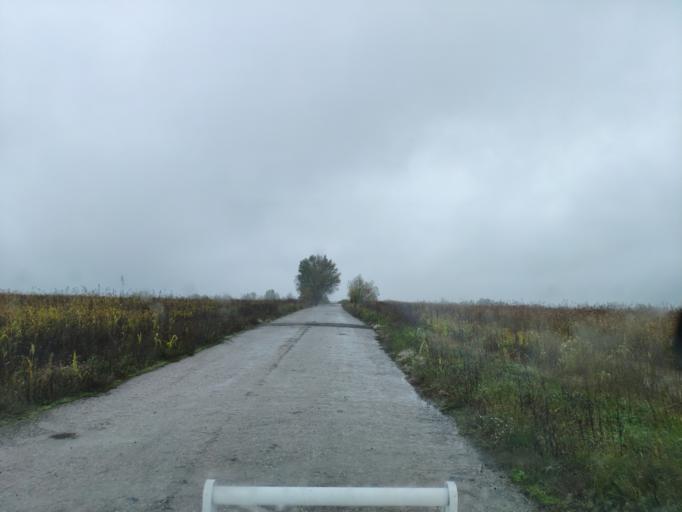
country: SK
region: Kosicky
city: Cierna nad Tisou
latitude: 48.4258
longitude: 21.9977
